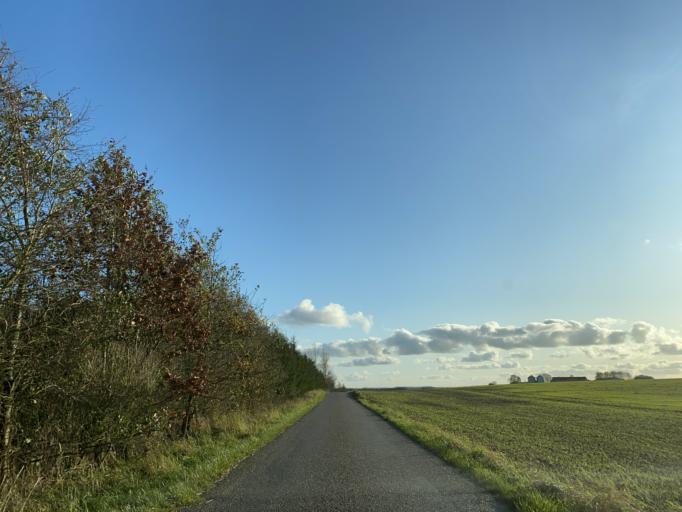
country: DK
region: Central Jutland
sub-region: Viborg Kommune
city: Bjerringbro
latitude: 56.3398
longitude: 9.7147
